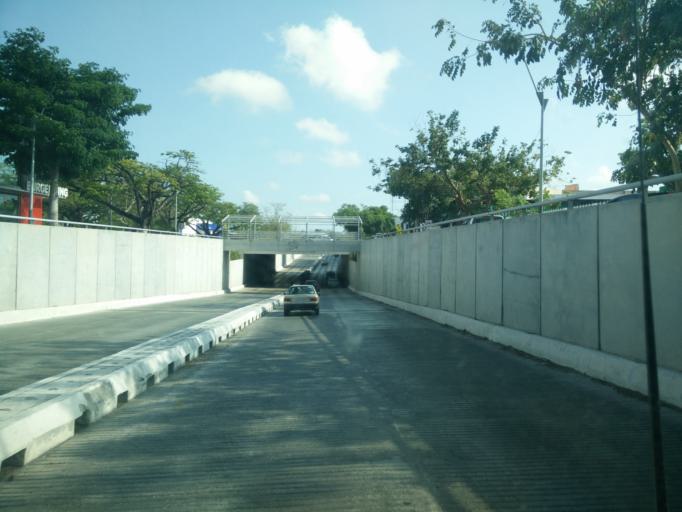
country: MX
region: Yucatan
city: Merida
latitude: 20.9978
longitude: -89.6160
